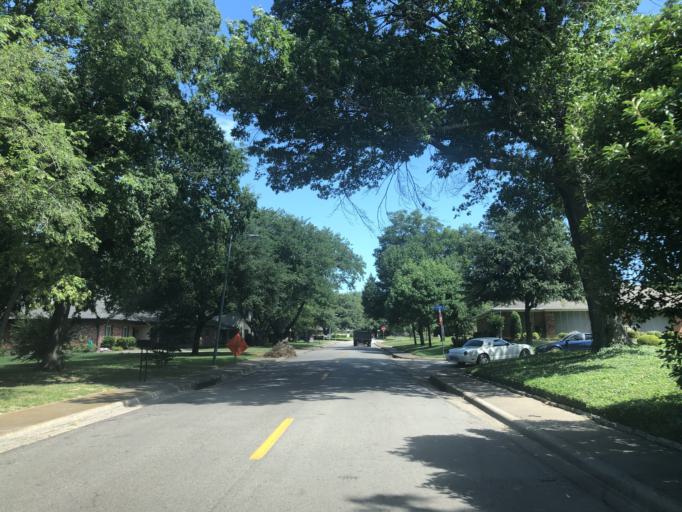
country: US
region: Texas
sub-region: Dallas County
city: Duncanville
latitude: 32.6501
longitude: -96.9289
